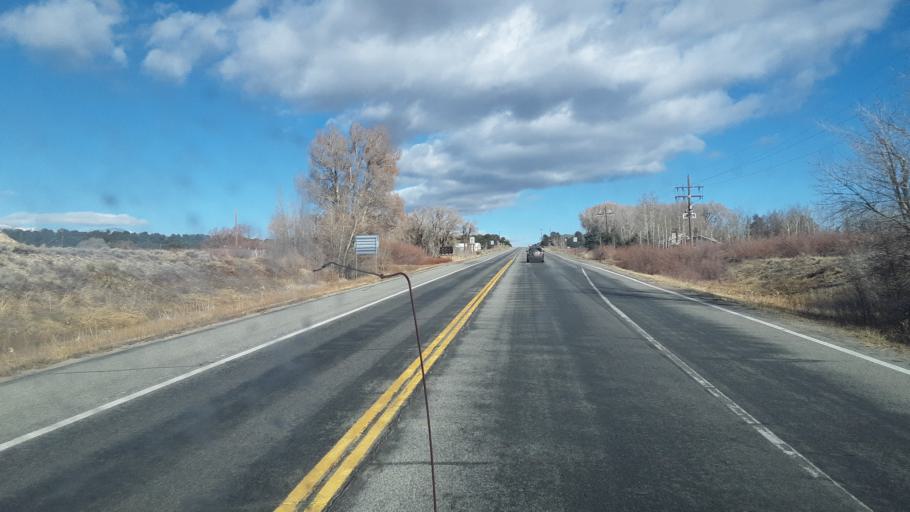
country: US
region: Colorado
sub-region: Chaffee County
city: Salida
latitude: 38.5253
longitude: -106.0798
